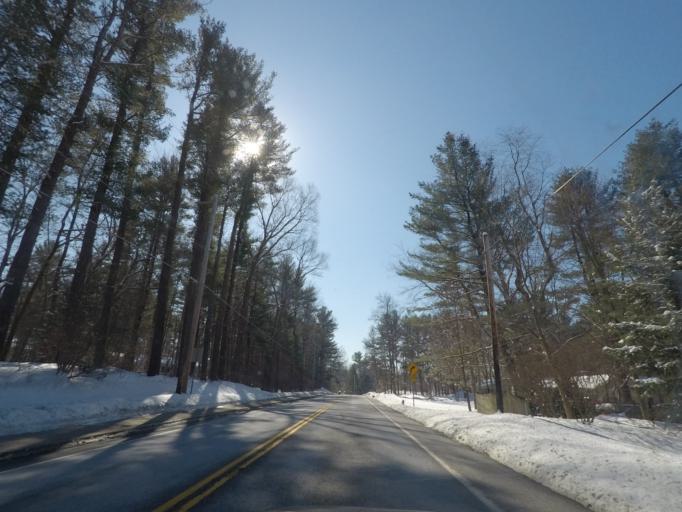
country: US
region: New York
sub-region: Saratoga County
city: Country Knolls
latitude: 42.9126
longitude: -73.8219
